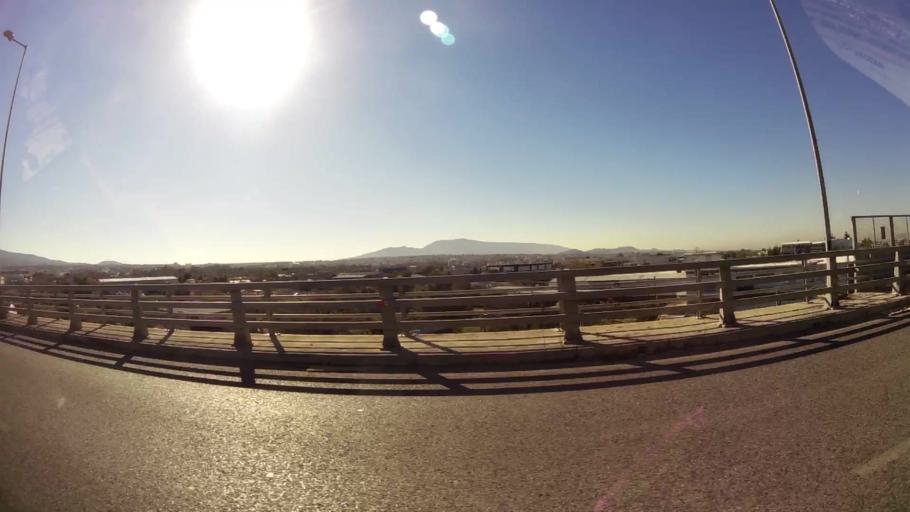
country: GR
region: Attica
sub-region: Nomarchia Athinas
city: Metamorfosi
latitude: 38.0923
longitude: 23.7685
